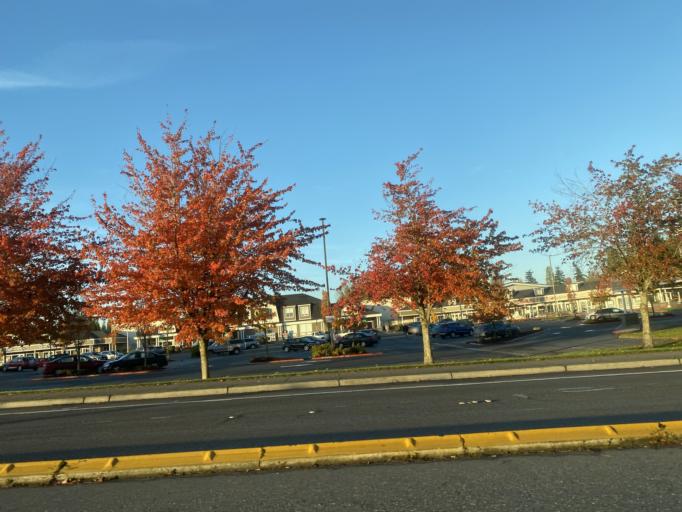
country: US
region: Washington
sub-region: Snohomish County
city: Mukilteo
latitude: 47.8917
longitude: -122.2862
